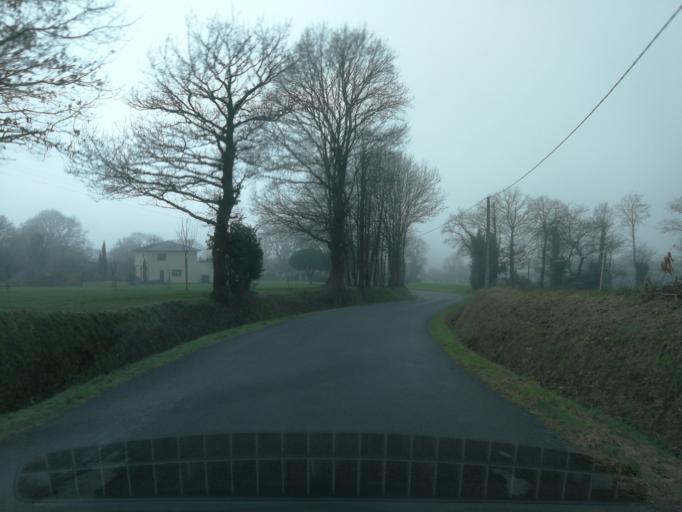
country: FR
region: Brittany
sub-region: Departement du Morbihan
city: La Vraie-Croix
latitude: 47.7361
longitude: -2.5036
